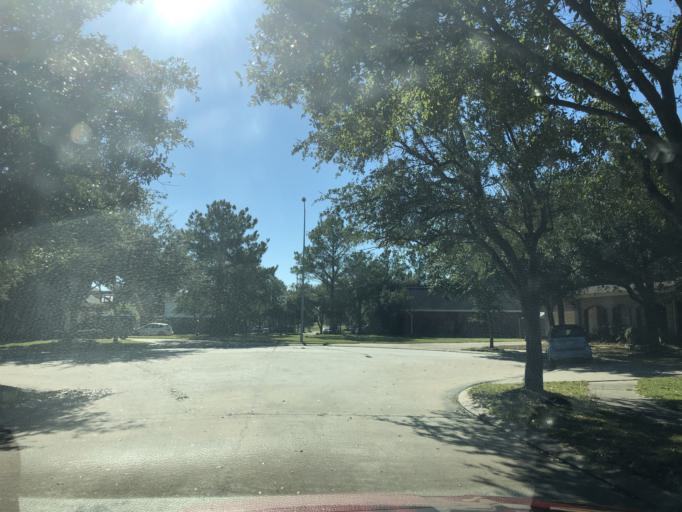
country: US
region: Texas
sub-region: Harris County
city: Oak Cliff Place
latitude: 29.9394
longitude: -95.6667
